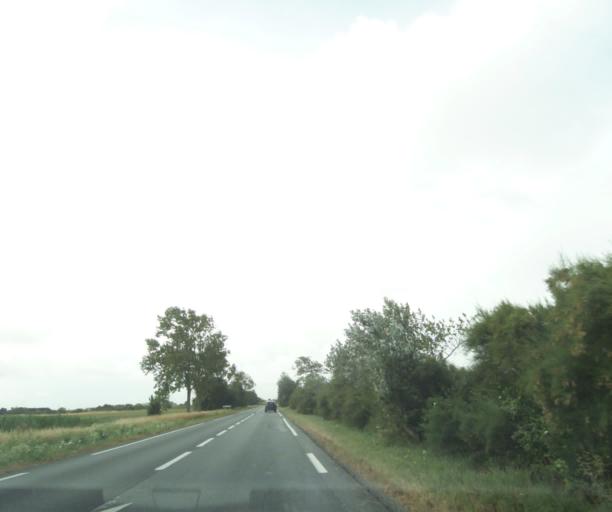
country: FR
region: Poitou-Charentes
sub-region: Departement de la Charente-Maritime
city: Andilly
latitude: 46.2573
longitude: -1.0666
